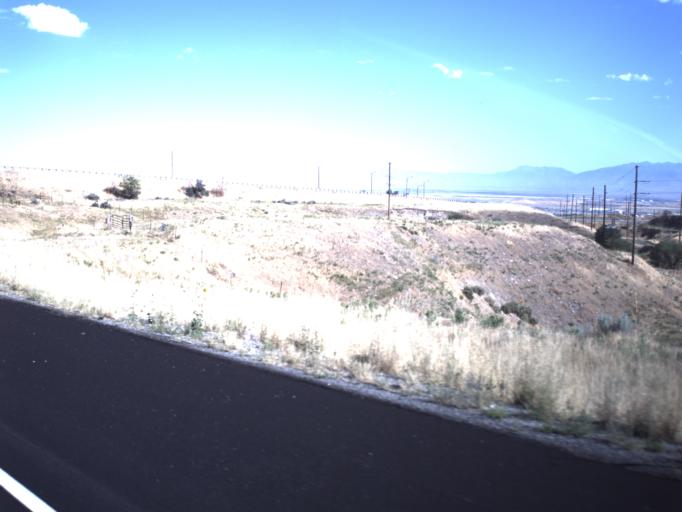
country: US
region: Utah
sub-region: Salt Lake County
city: Magna
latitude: 40.6639
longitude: -112.0900
